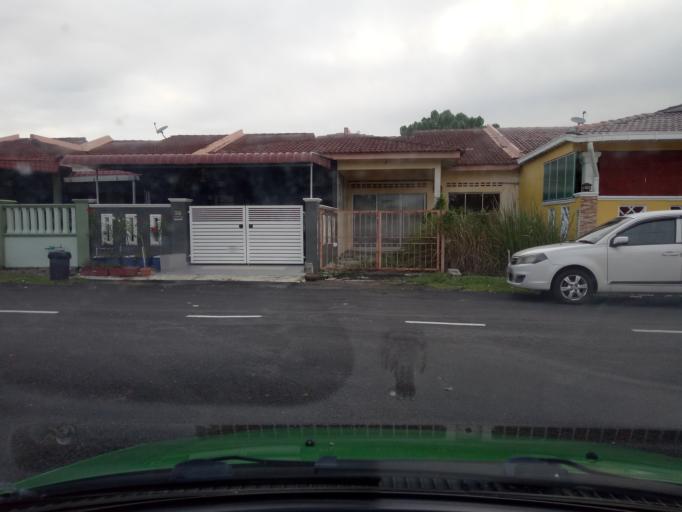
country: MY
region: Selangor
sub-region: Hulu Langat
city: Semenyih
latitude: 2.9288
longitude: 101.8619
